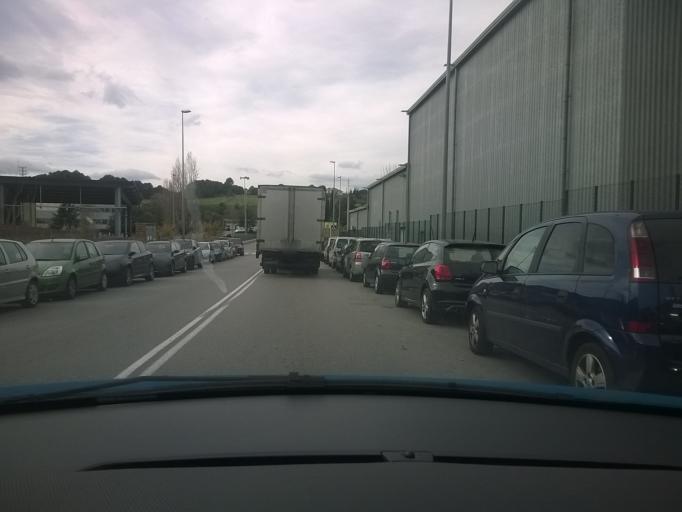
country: ES
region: Catalonia
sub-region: Provincia de Barcelona
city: Rubi
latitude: 41.5072
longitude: 2.0346
